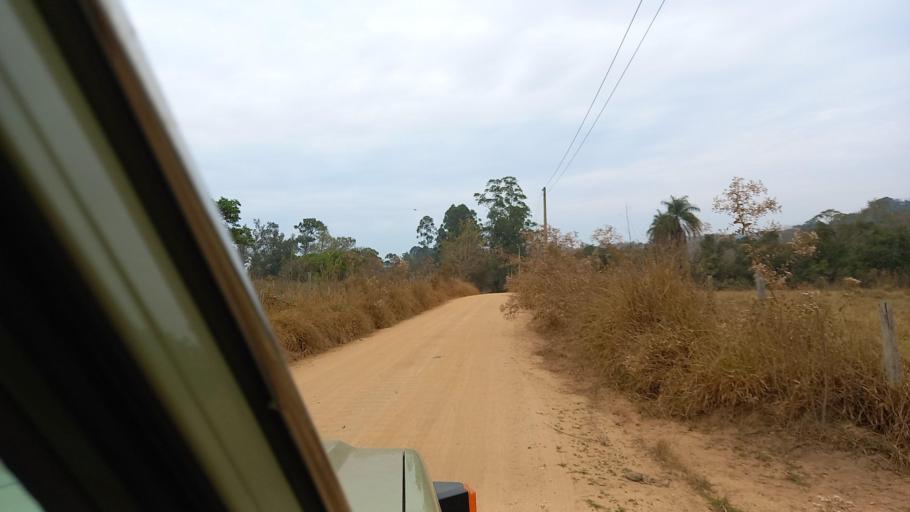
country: BR
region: Sao Paulo
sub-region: Moji-Guacu
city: Mogi-Gaucu
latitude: -22.3055
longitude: -46.8330
